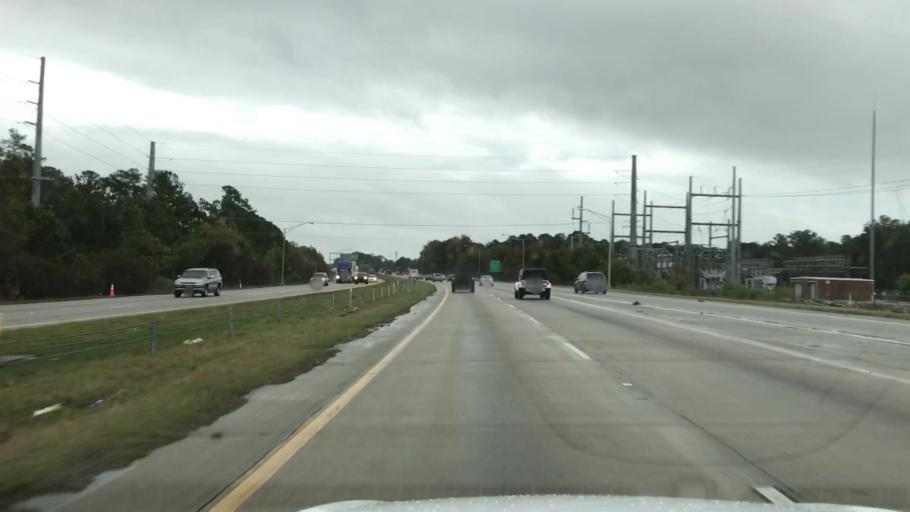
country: US
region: South Carolina
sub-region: Charleston County
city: North Charleston
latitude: 32.8760
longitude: -79.9277
